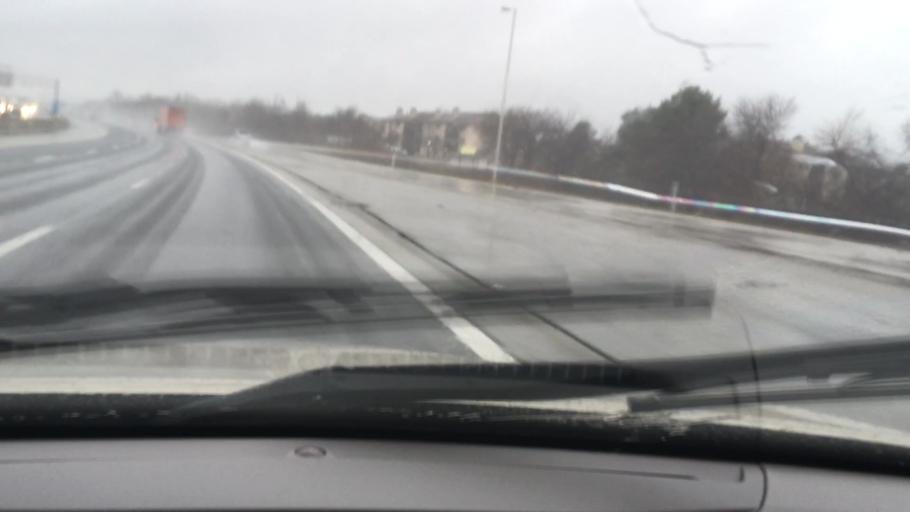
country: US
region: Indiana
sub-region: Hamilton County
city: Carmel
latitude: 39.9123
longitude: -86.0813
